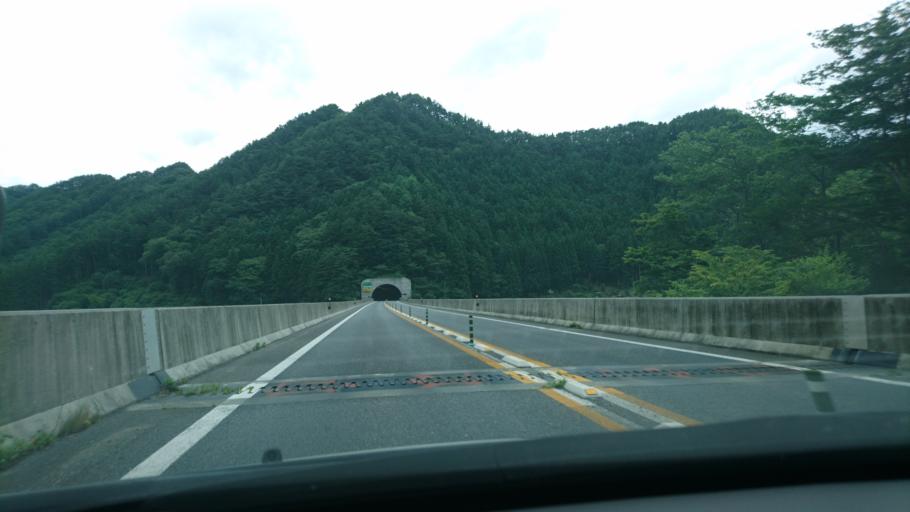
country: JP
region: Iwate
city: Kamaishi
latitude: 39.3229
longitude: 141.8802
